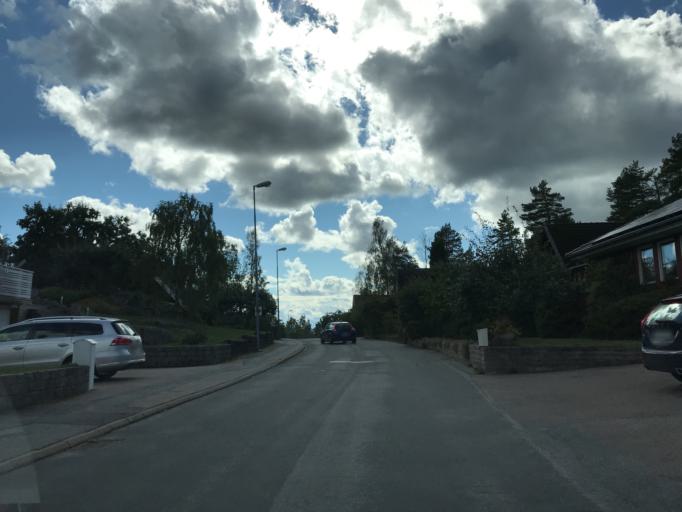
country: SE
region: Stockholm
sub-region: Sollentuna Kommun
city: Sollentuna
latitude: 59.4628
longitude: 17.9455
